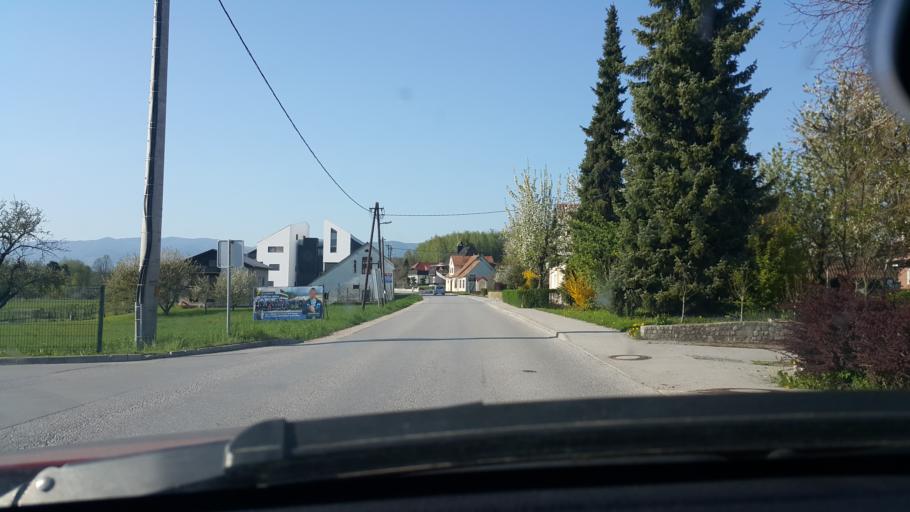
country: SI
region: Celje
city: Ljubecna
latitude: 46.2591
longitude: 15.3218
